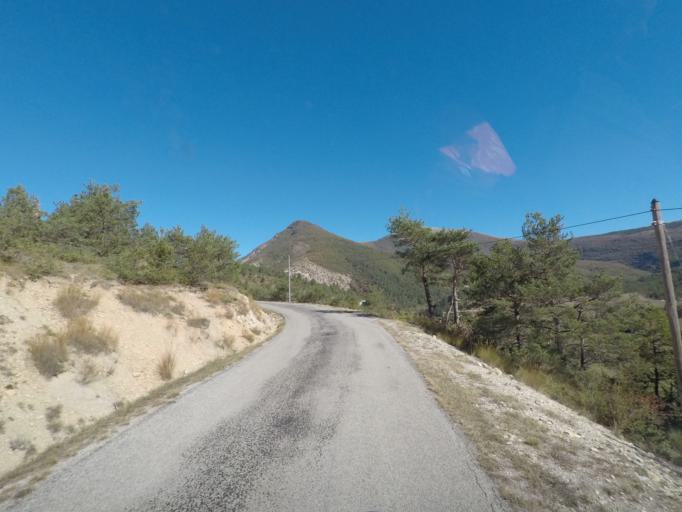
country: FR
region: Rhone-Alpes
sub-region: Departement de la Drome
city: Die
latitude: 44.5579
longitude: 5.3226
